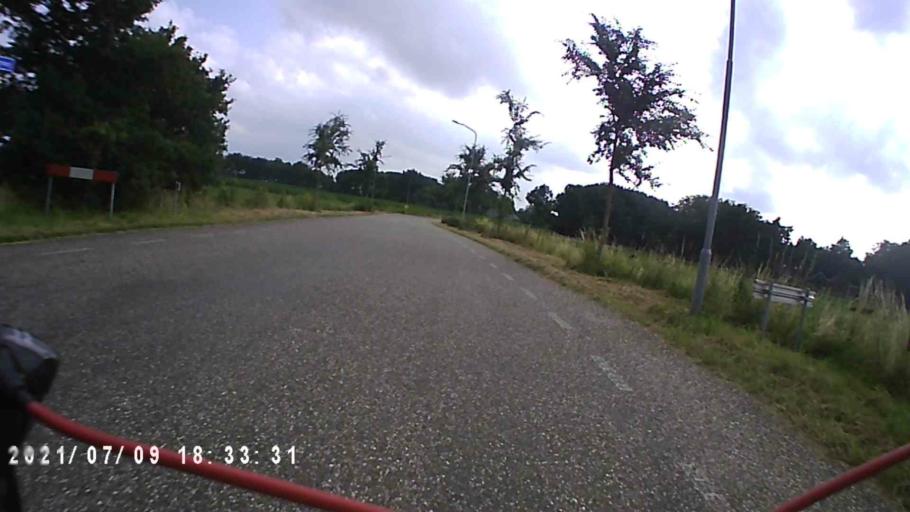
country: NL
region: Groningen
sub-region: Gemeente Pekela
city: Oude Pekela
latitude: 53.0727
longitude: 6.9676
